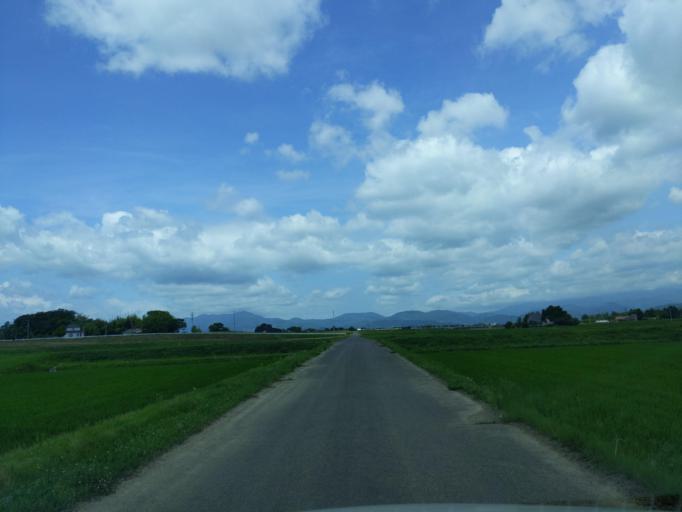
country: JP
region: Fukushima
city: Koriyama
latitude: 37.4449
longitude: 140.3672
